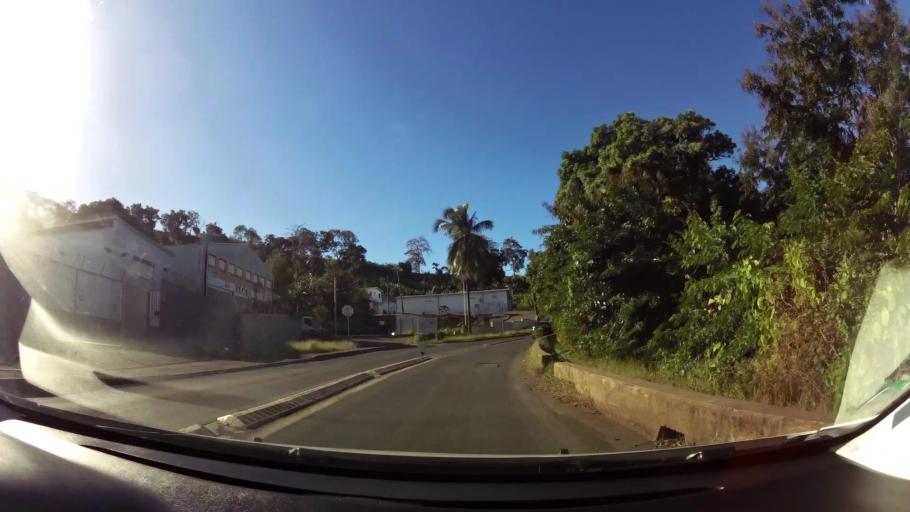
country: YT
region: Mamoudzou
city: Mamoudzou
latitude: -12.7606
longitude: 45.2266
